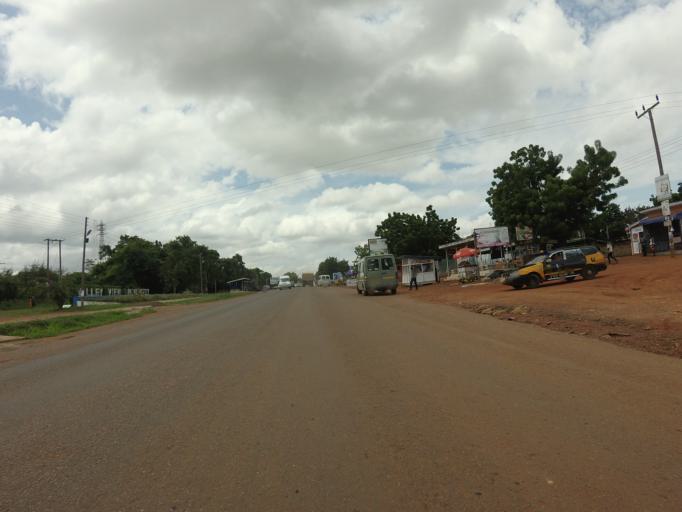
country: GH
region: Eastern
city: Aburi
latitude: 5.7996
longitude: -0.1271
